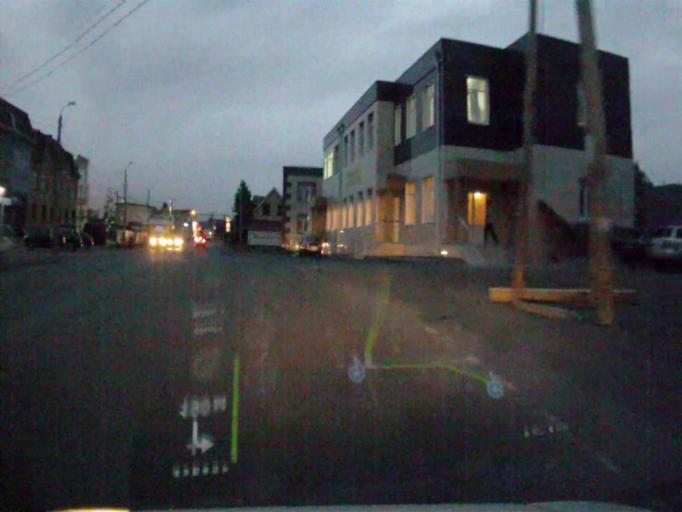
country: RU
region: Chelyabinsk
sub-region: Gorod Chelyabinsk
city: Chelyabinsk
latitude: 55.1558
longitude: 61.3005
